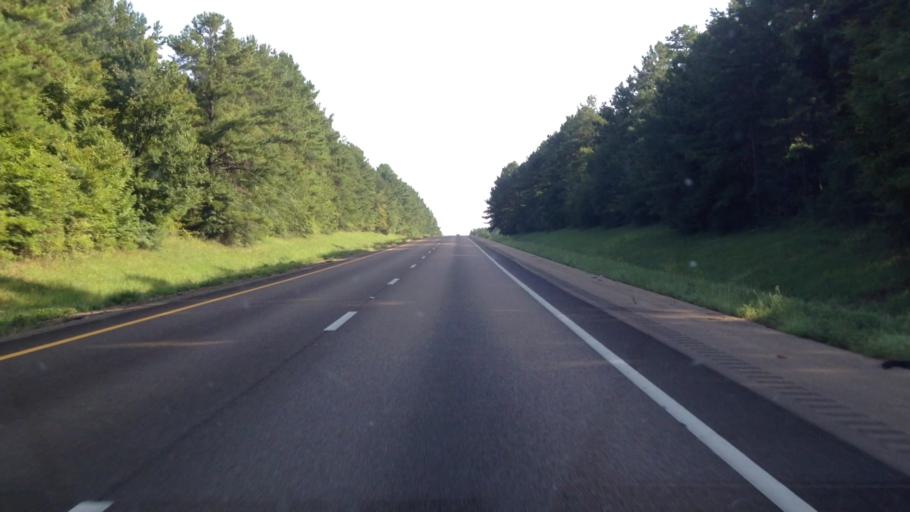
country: US
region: Mississippi
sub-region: Pike County
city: Summit
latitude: 31.3825
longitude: -90.4791
